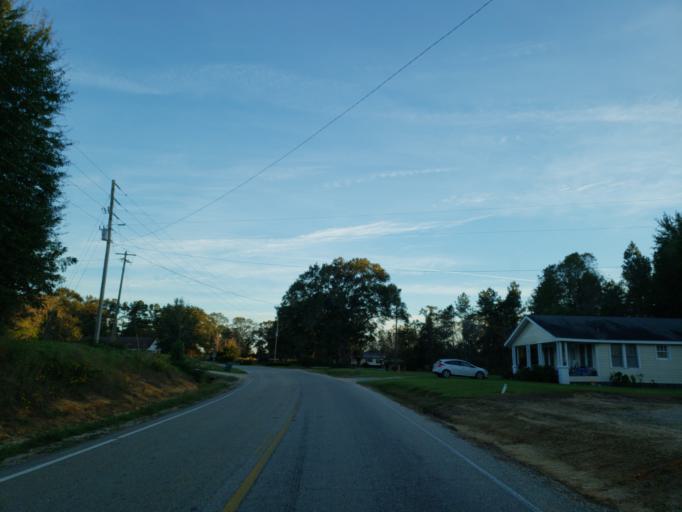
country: US
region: Mississippi
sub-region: Wayne County
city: Belmont
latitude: 31.4284
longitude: -88.4725
